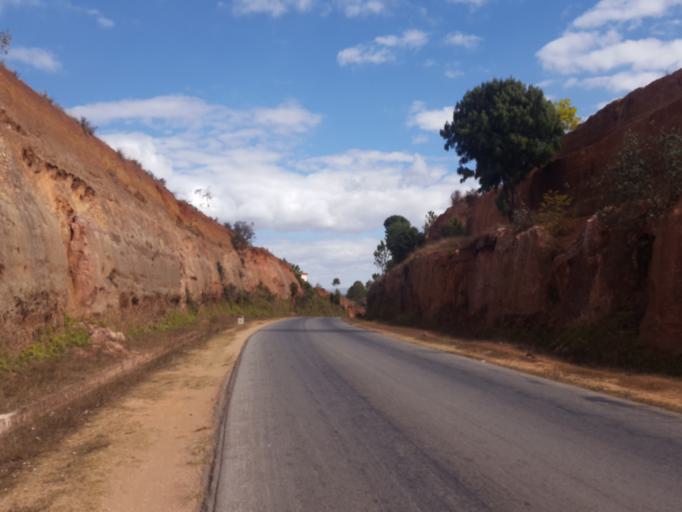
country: MG
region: Analamanga
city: Antananarivo
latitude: -18.9531
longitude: 47.3600
